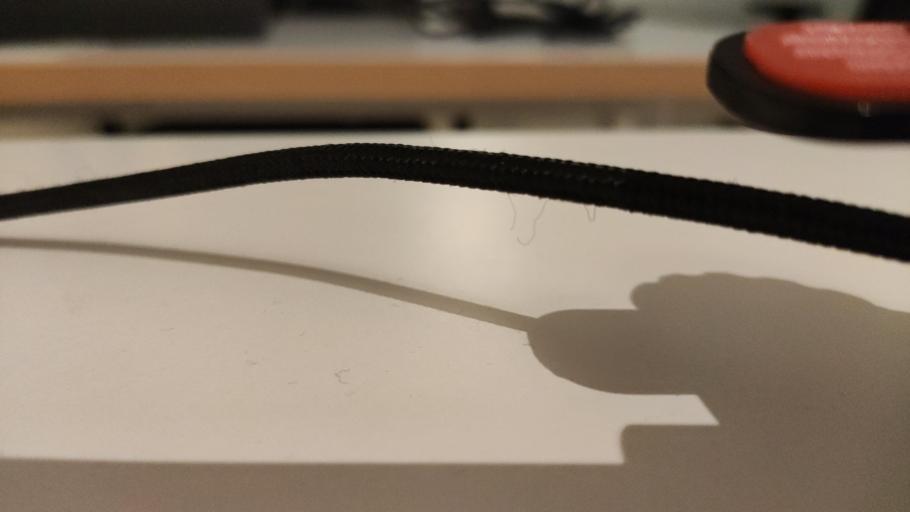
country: RU
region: Moskovskaya
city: Novoye
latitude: 55.6376
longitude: 38.9290
